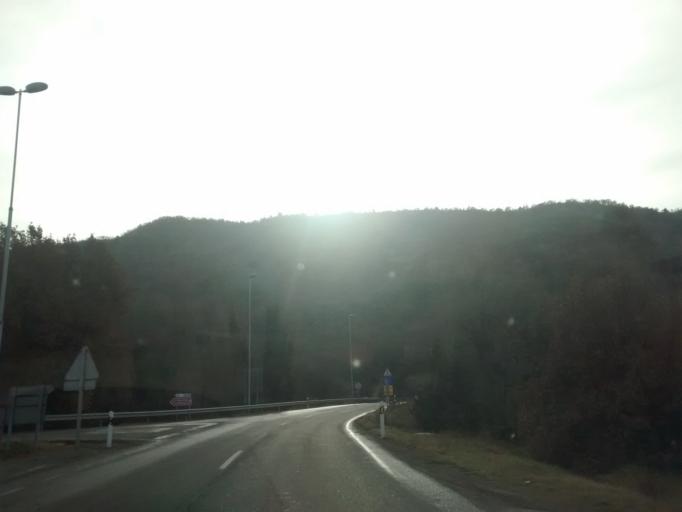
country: ES
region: Aragon
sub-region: Provincia de Huesca
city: Bailo
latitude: 42.5563
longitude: -0.7862
